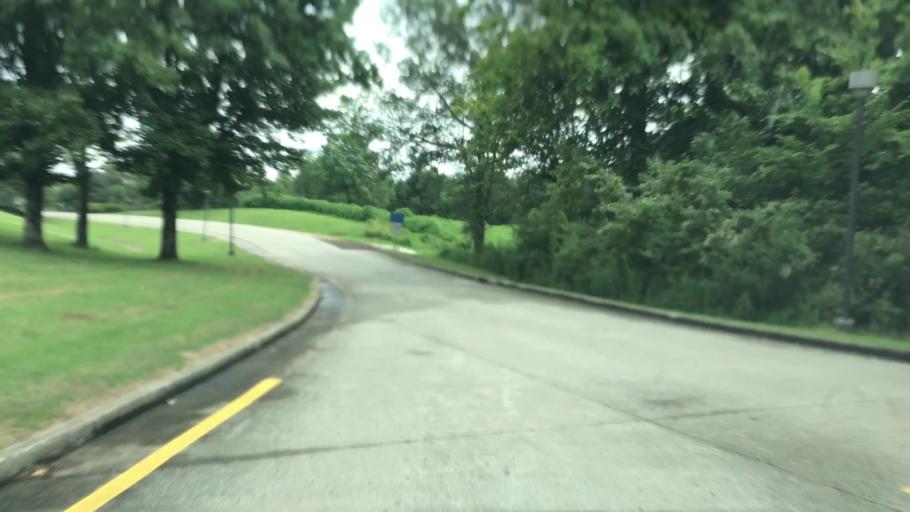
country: US
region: Tennessee
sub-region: Dyer County
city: Dyersburg
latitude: 36.0705
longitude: -89.4682
